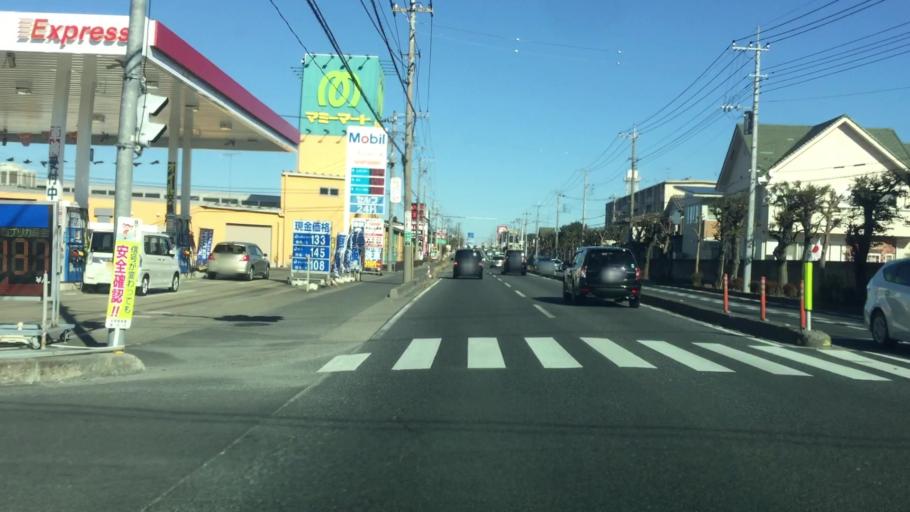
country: JP
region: Saitama
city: Hasuda
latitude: 35.9837
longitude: 139.6444
